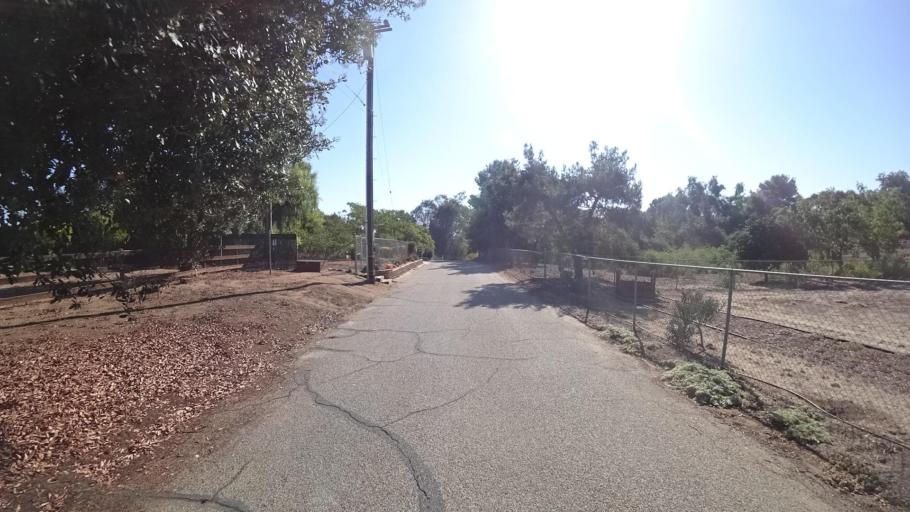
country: US
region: California
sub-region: San Diego County
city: Hidden Meadows
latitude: 33.2361
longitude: -117.1185
